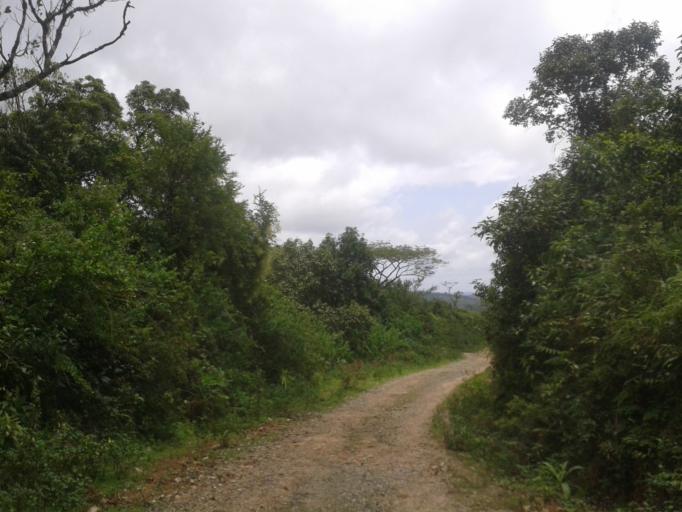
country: IN
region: Karnataka
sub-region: Chikmagalur
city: Mudigere
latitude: 12.9866
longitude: 75.6143
